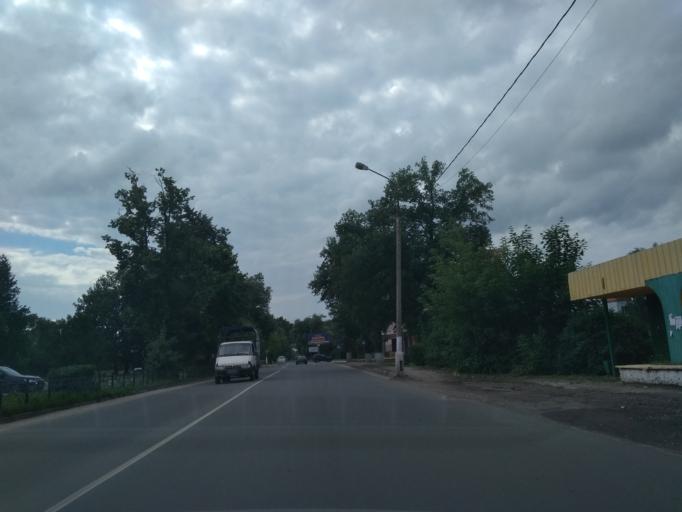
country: RU
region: Moskovskaya
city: Orekhovo-Zuyevo
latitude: 55.7966
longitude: 38.9419
